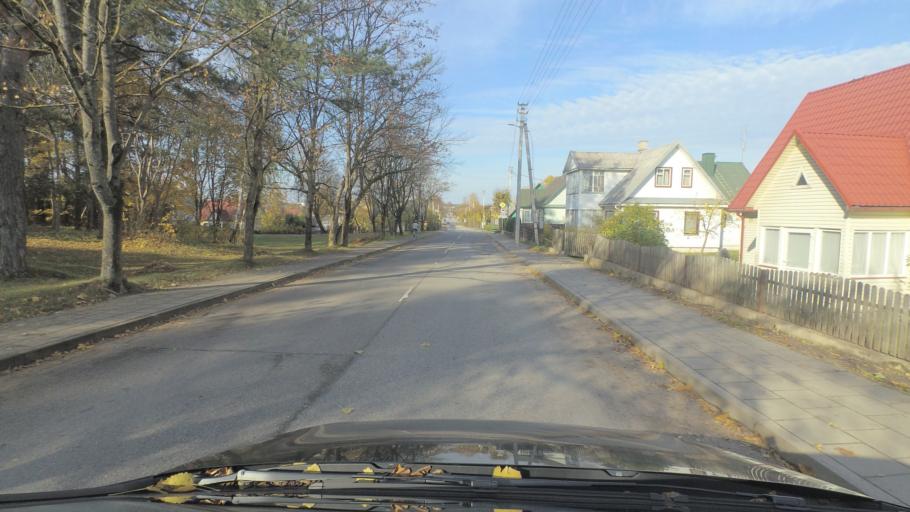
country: LT
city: Ignalina
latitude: 55.3416
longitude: 26.1759
